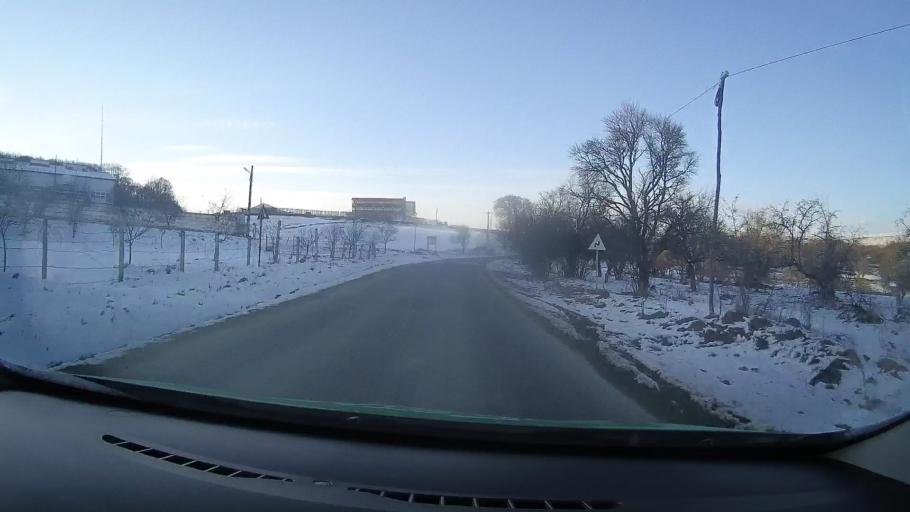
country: RO
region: Sibiu
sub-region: Oras Agnita
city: Ruja
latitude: 45.9839
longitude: 24.6872
